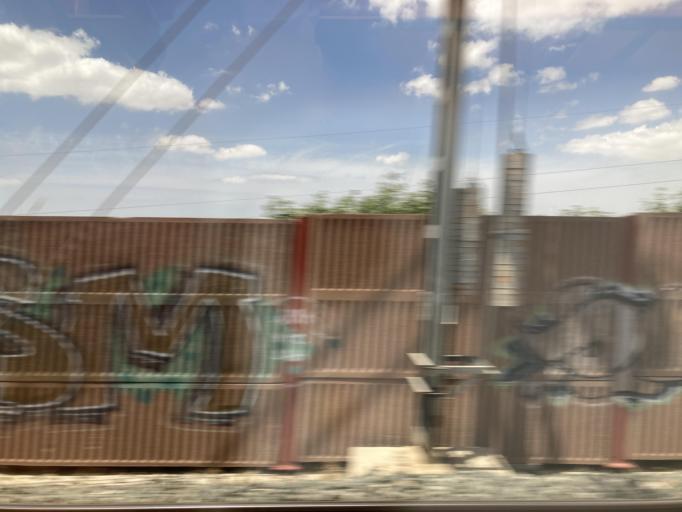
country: ES
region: Andalusia
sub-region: Provincia de Cadiz
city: Jerez de la Frontera
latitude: 36.6695
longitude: -6.1238
